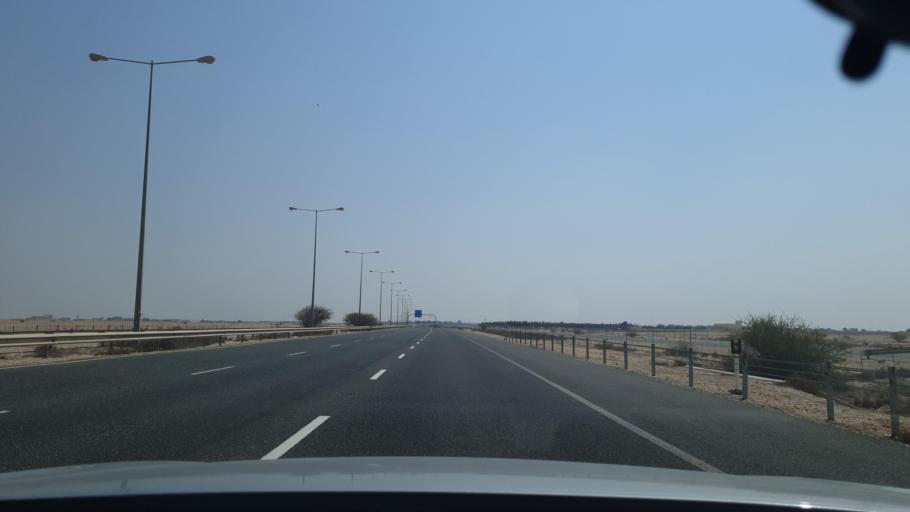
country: QA
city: Al Ghuwayriyah
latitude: 25.7957
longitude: 51.3870
